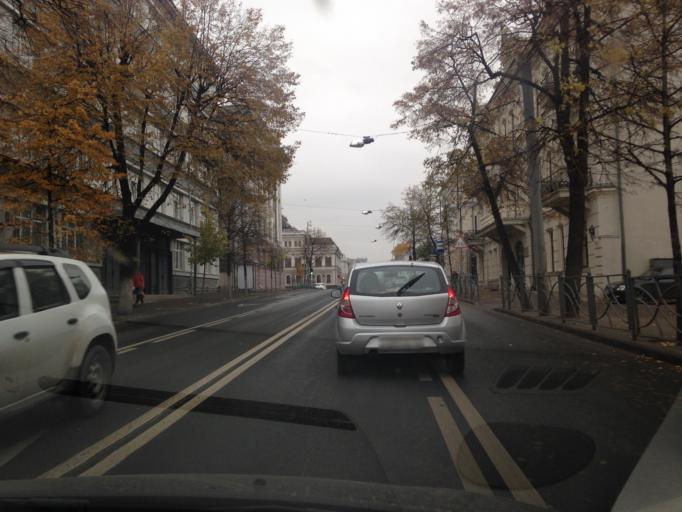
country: RU
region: Tatarstan
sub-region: Gorod Kazan'
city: Kazan
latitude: 55.7964
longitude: 49.1226
